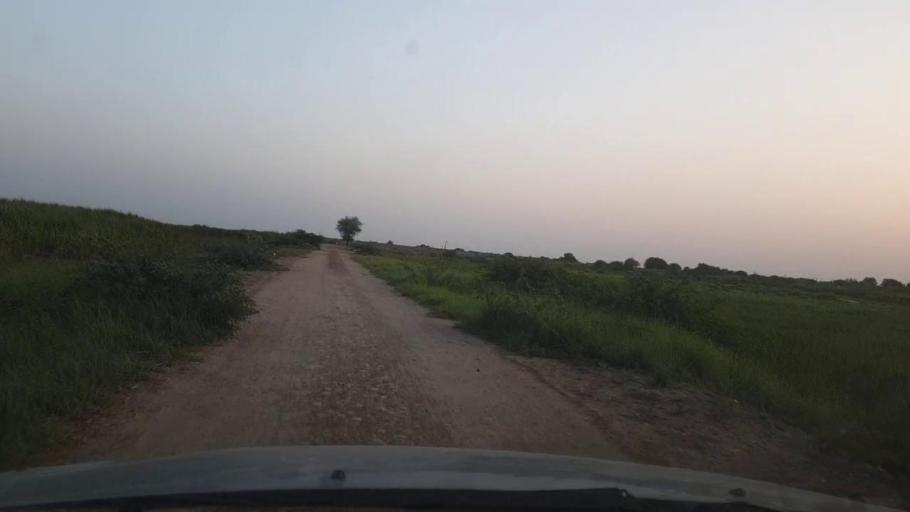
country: PK
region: Sindh
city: Digri
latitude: 25.1144
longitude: 68.9925
